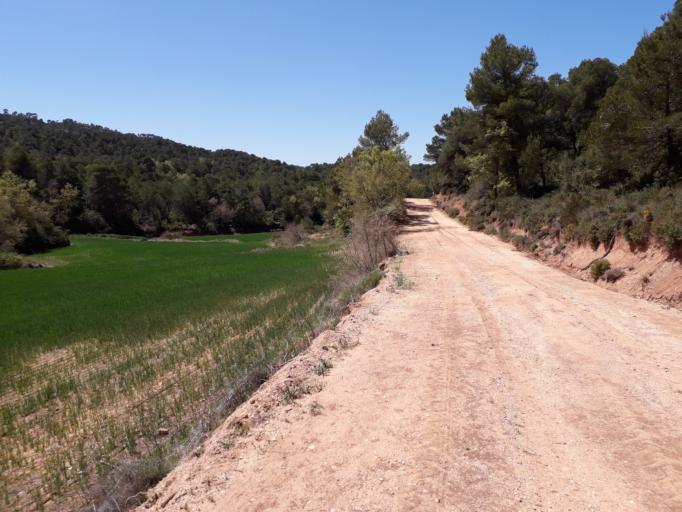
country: ES
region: Catalonia
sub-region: Provincia de Barcelona
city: Bellprat
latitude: 41.5204
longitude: 1.4569
